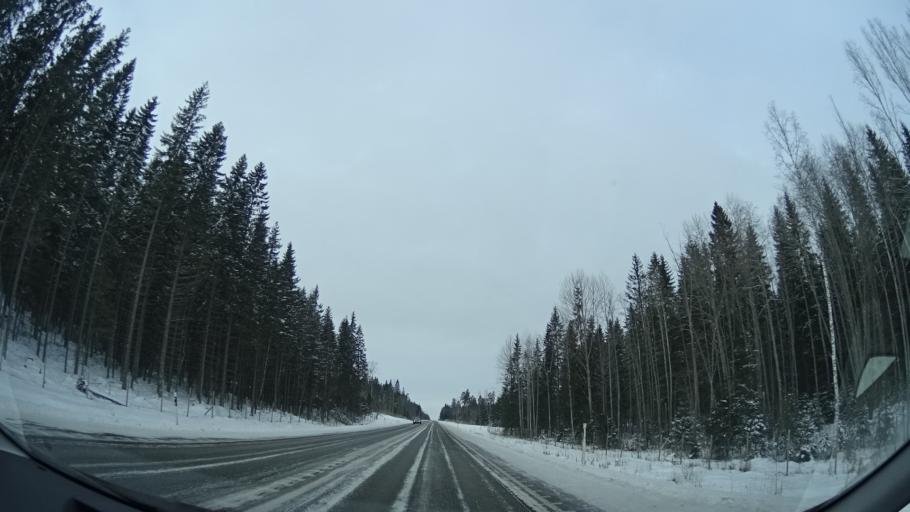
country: FI
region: Uusimaa
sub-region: Helsinki
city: Kaerkoelae
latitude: 60.6241
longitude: 23.9763
